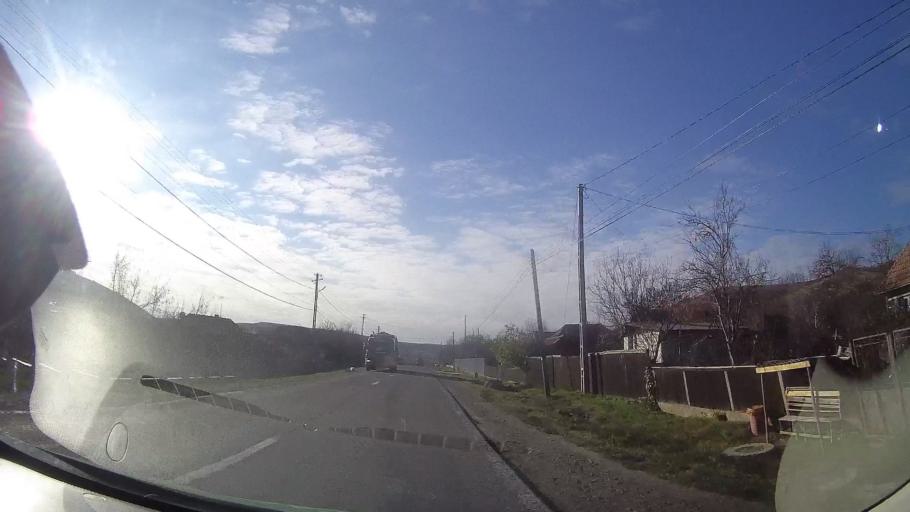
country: RO
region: Cluj
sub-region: Comuna Caianu
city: Caianu
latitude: 46.7959
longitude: 23.9135
